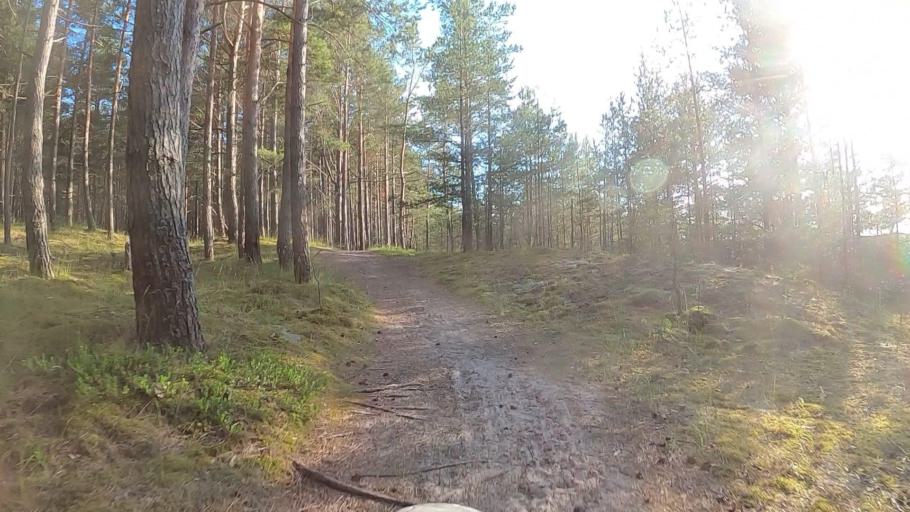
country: LV
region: Carnikava
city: Carnikava
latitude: 57.1229
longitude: 24.2093
